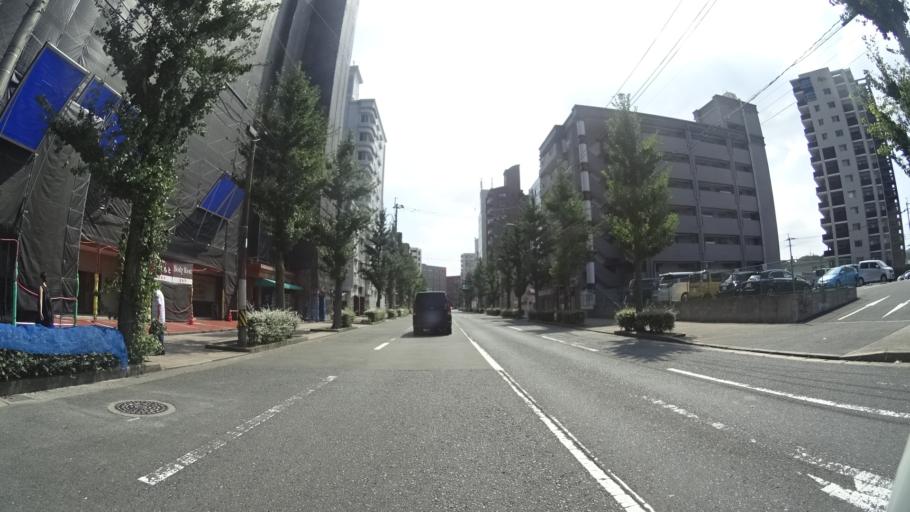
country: JP
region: Fukuoka
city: Kitakyushu
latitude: 33.8802
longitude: 130.8590
